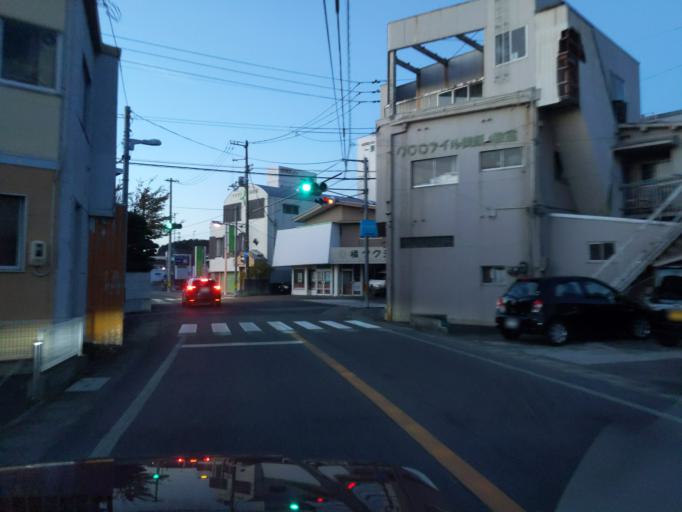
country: JP
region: Tokushima
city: Anan
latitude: 33.8887
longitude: 134.6527
